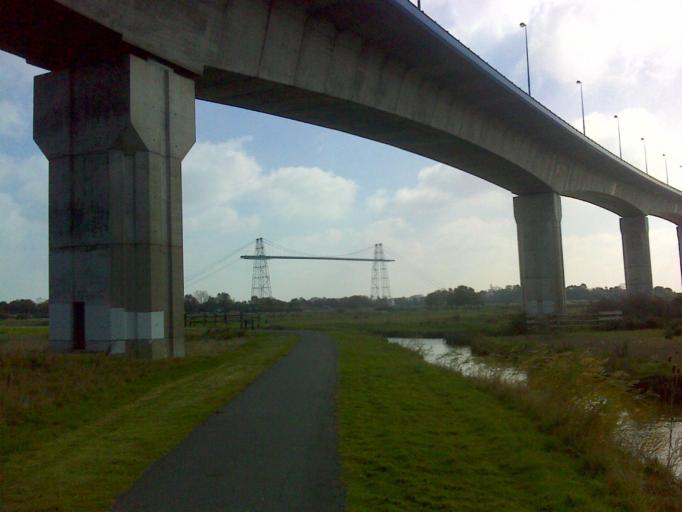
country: FR
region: Poitou-Charentes
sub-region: Departement de la Charente-Maritime
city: Rochefort
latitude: 45.9194
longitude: -0.9684
